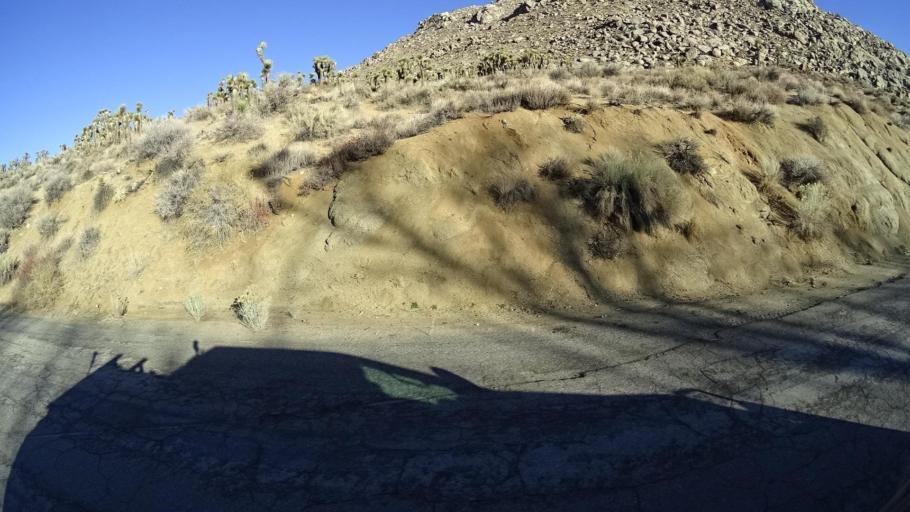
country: US
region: California
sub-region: Kern County
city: Weldon
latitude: 35.5006
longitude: -118.2038
